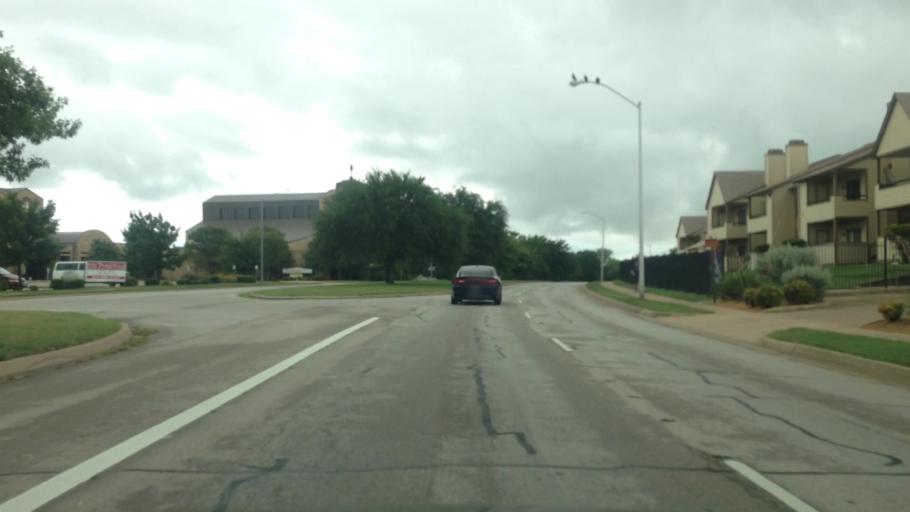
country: US
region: Texas
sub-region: Tarrant County
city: Edgecliff Village
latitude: 32.6329
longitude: -97.3894
